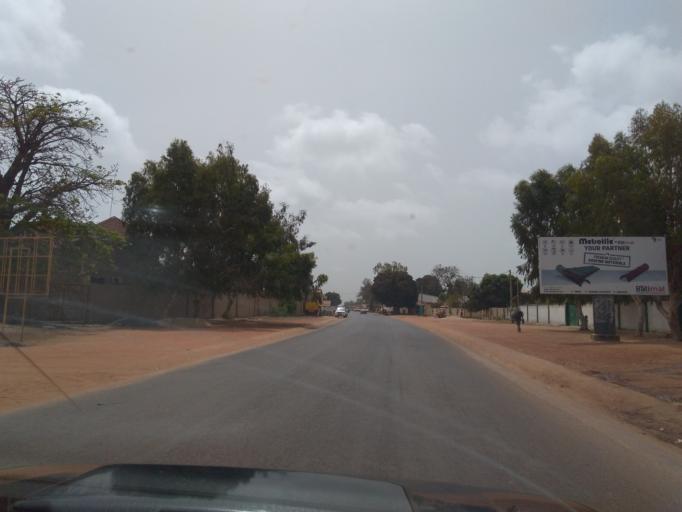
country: GM
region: Western
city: Sukuta
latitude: 13.4409
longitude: -16.7160
